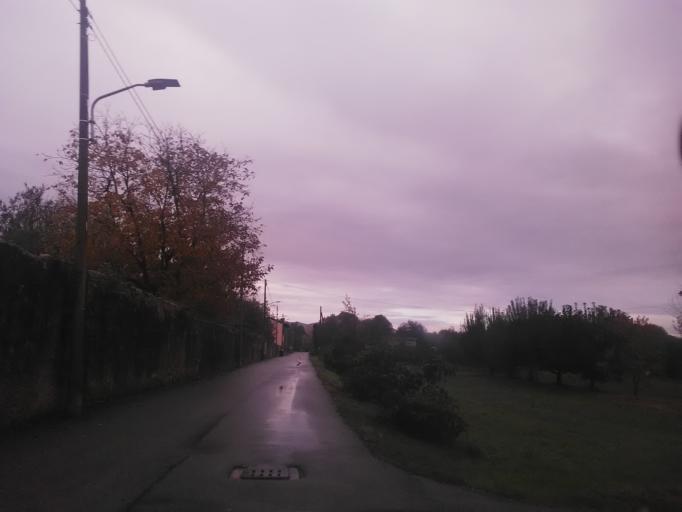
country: IT
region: Piedmont
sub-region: Provincia di Vercelli
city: Gattinara
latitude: 45.6164
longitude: 8.3749
